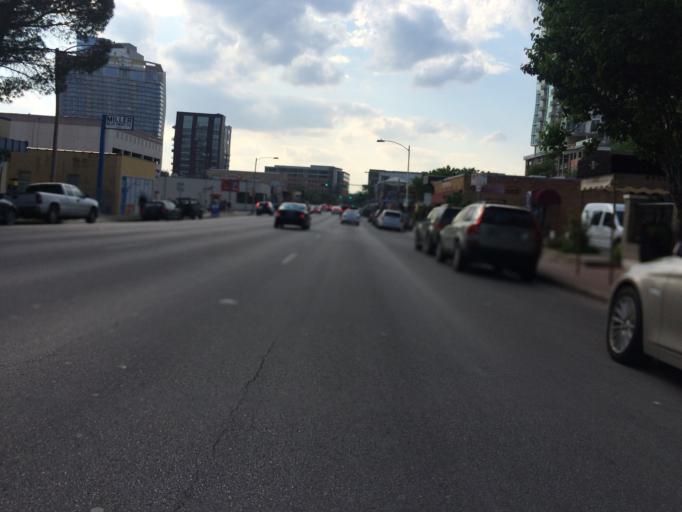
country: US
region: Texas
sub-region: Travis County
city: Austin
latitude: 30.2694
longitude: -97.7473
